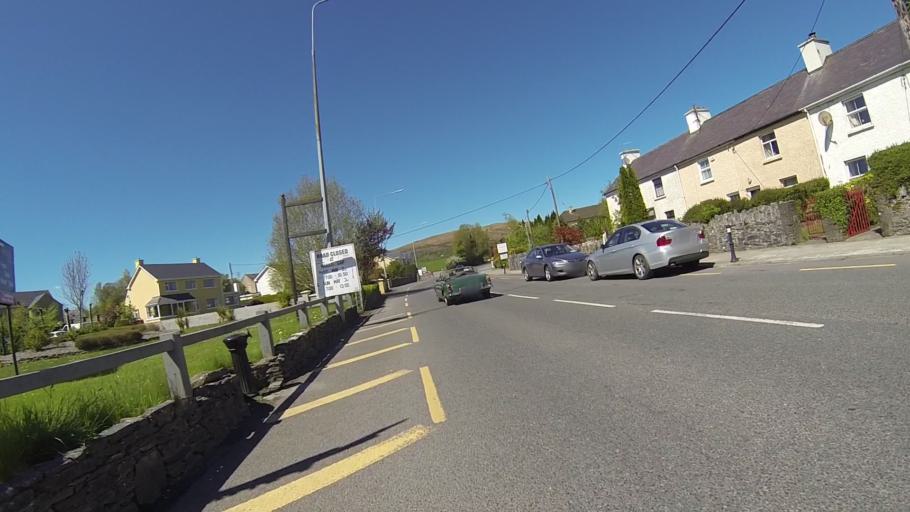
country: IE
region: Munster
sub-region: Ciarrai
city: Kenmare
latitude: 51.8840
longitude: -9.5904
